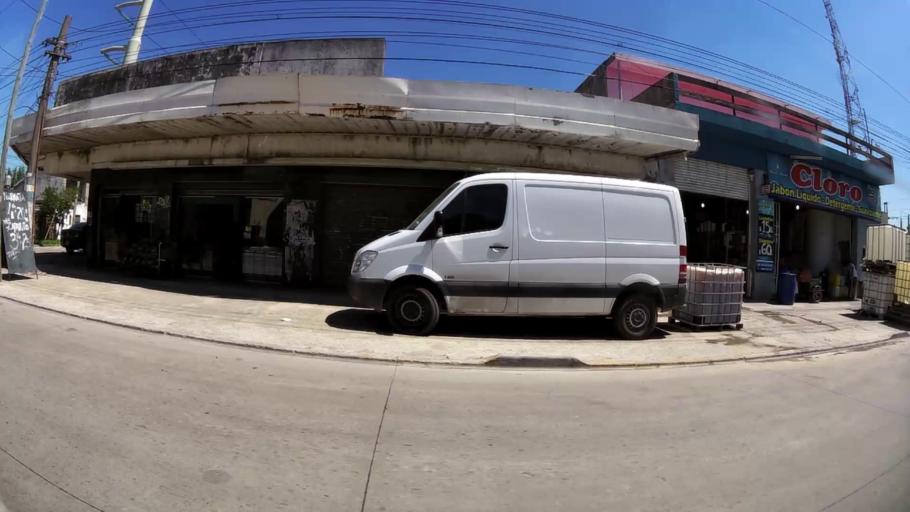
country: AR
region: Buenos Aires
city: Ituzaingo
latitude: -34.6804
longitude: -58.6718
